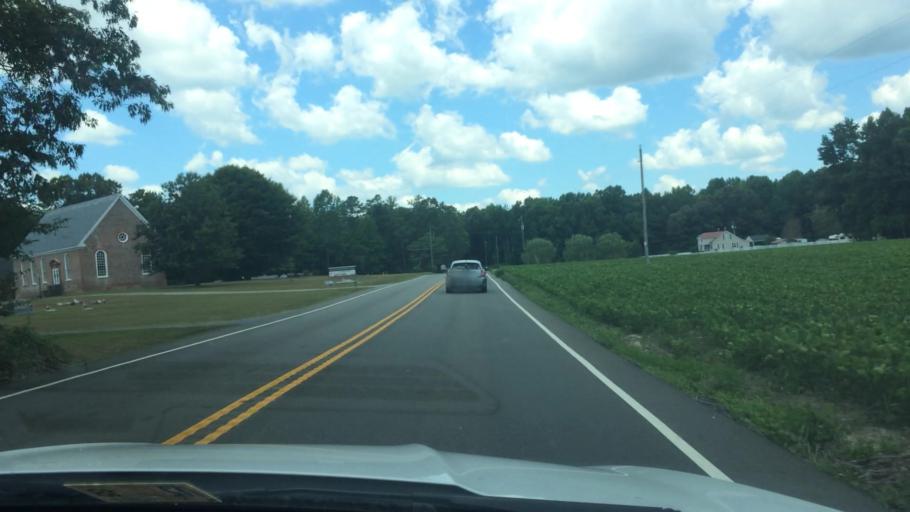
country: US
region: Virginia
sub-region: King William County
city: West Point
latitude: 37.6024
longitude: -76.7696
